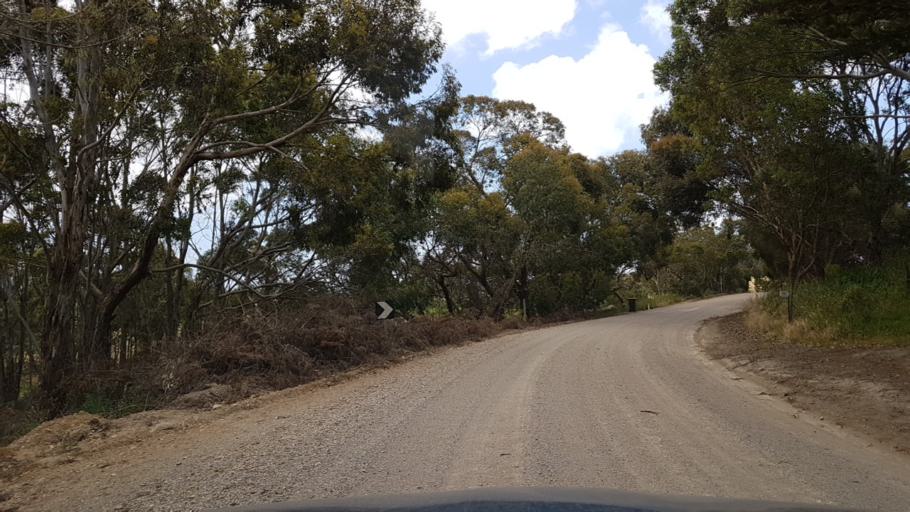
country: AU
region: South Australia
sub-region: Onkaparinga
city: Aldinga
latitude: -35.3747
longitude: 138.5131
